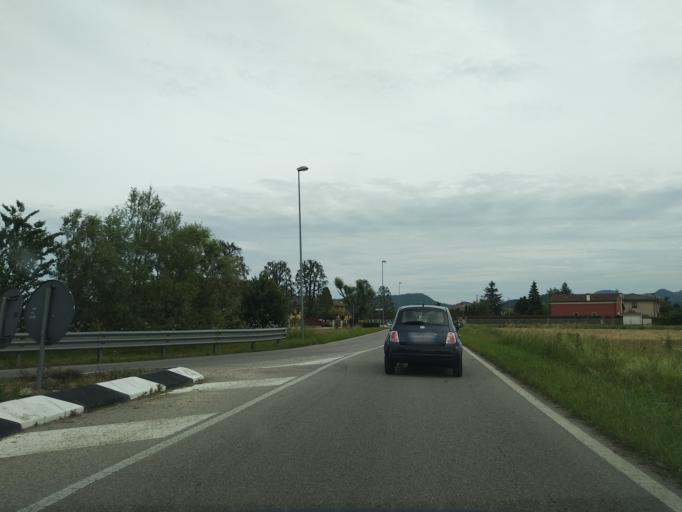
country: IT
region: Veneto
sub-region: Provincia di Padova
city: Montemerlo
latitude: 45.3966
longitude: 11.6974
